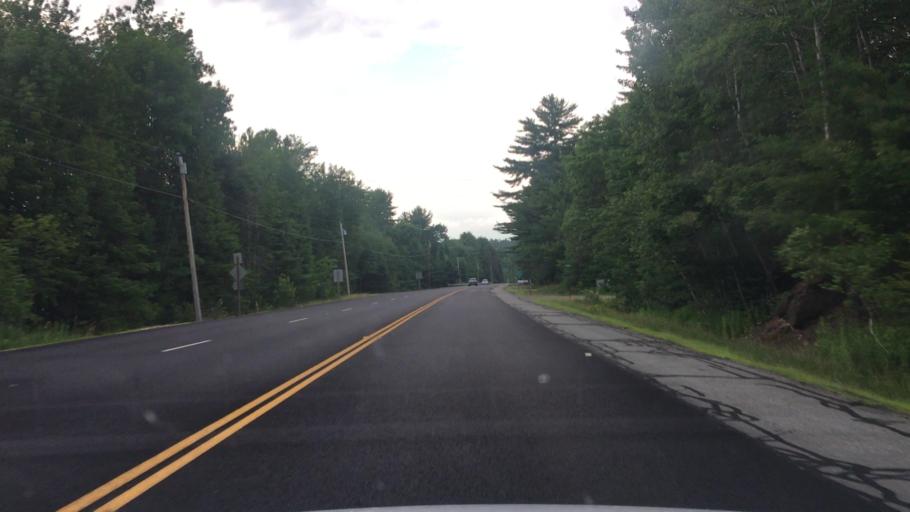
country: US
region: Maine
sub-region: Waldo County
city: Palermo
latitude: 44.3992
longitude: -69.4754
